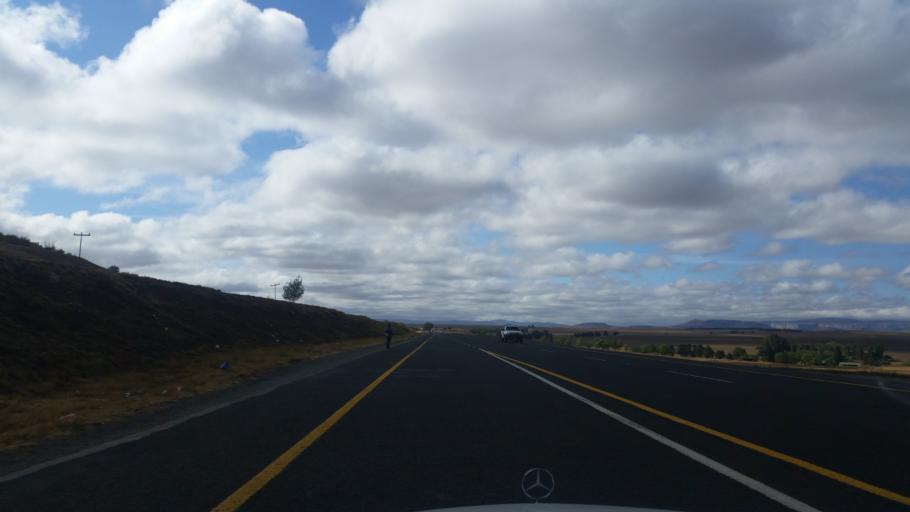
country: ZA
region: Orange Free State
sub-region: Thabo Mofutsanyana District Municipality
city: Phuthaditjhaba
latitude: -28.3067
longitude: 28.7104
